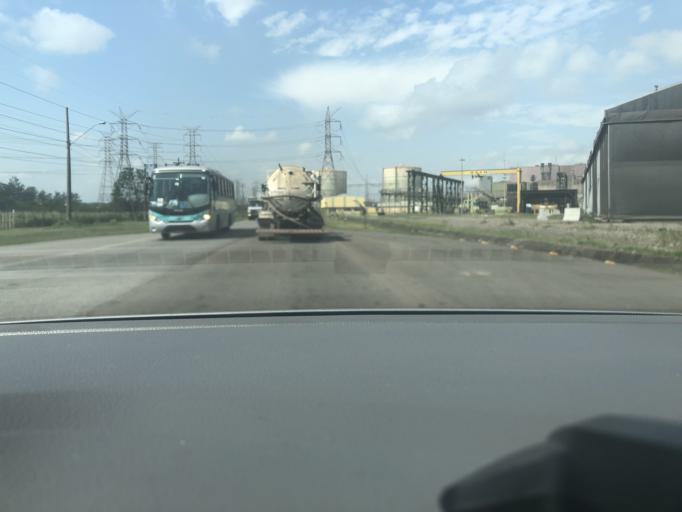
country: BR
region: Rio de Janeiro
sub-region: Itaguai
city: Itaguai
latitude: -22.9118
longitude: -43.7471
